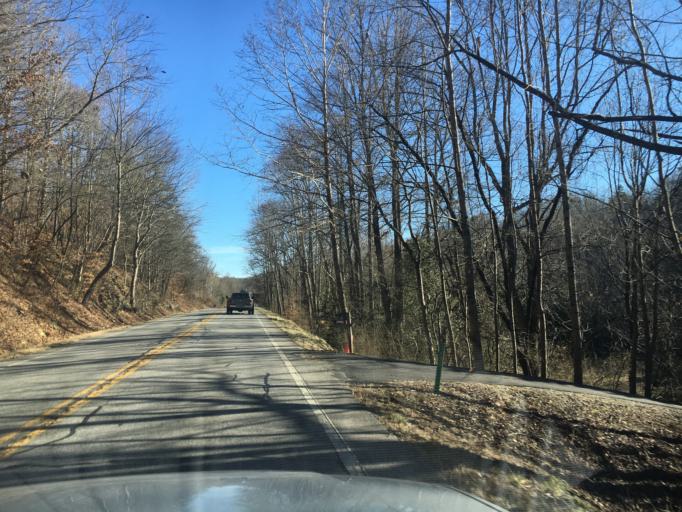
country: US
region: Georgia
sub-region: Union County
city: Blairsville
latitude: 34.8309
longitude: -83.9282
